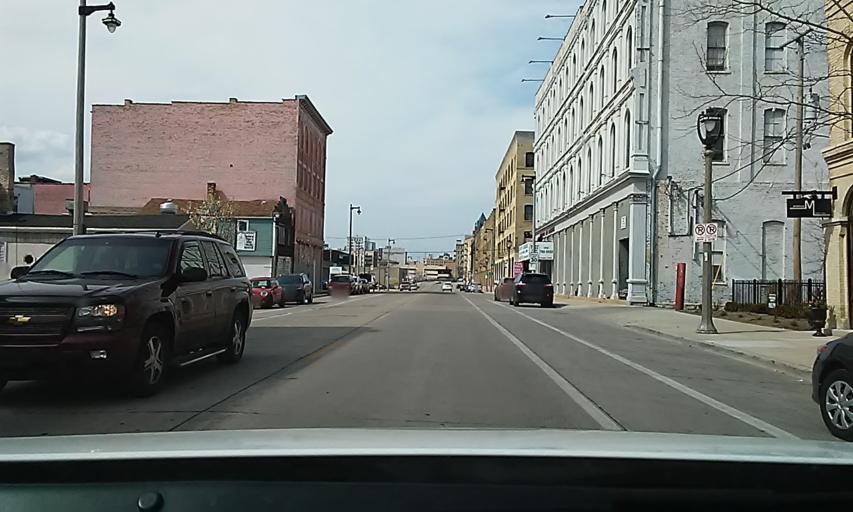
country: US
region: Wisconsin
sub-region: Milwaukee County
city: Milwaukee
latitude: 43.0296
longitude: -87.9127
